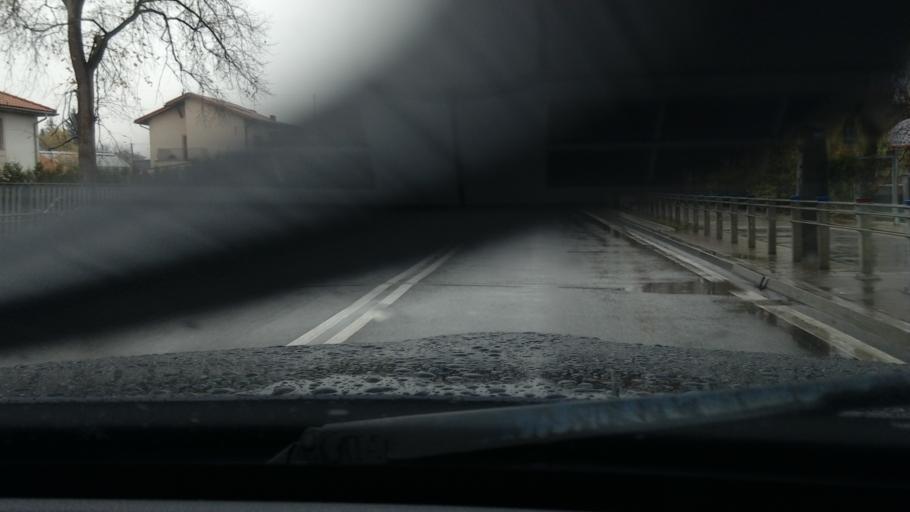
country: PL
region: Lodz Voivodeship
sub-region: Skierniewice
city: Skierniewice
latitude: 51.9535
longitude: 20.1345
